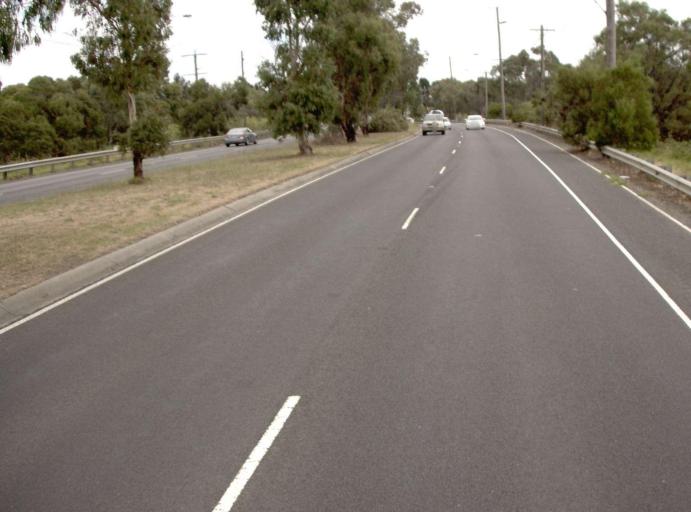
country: AU
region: Victoria
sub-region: Knox
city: Rowville
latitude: -37.9492
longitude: 145.2278
